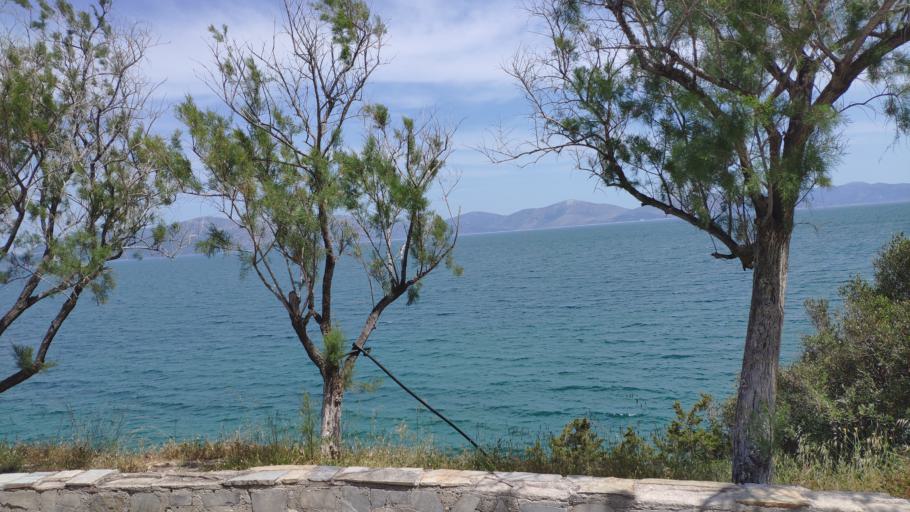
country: GR
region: Attica
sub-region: Nomarchia Anatolikis Attikis
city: Grammatiko
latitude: 38.2639
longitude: 23.9755
